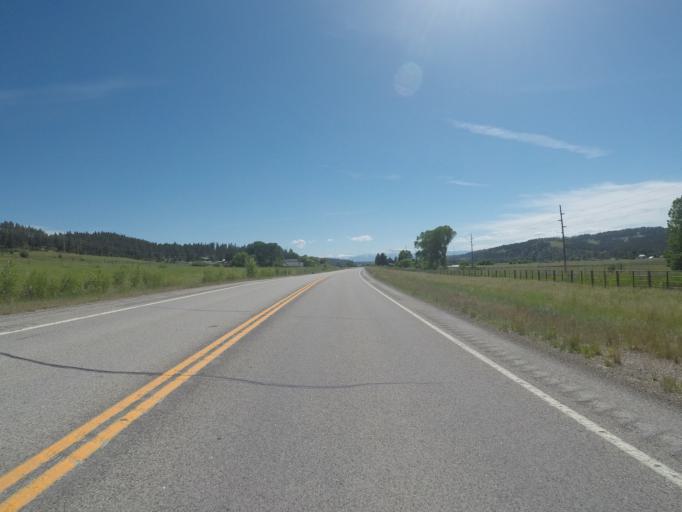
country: US
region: Montana
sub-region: Stillwater County
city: Columbus
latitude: 45.6115
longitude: -109.2813
